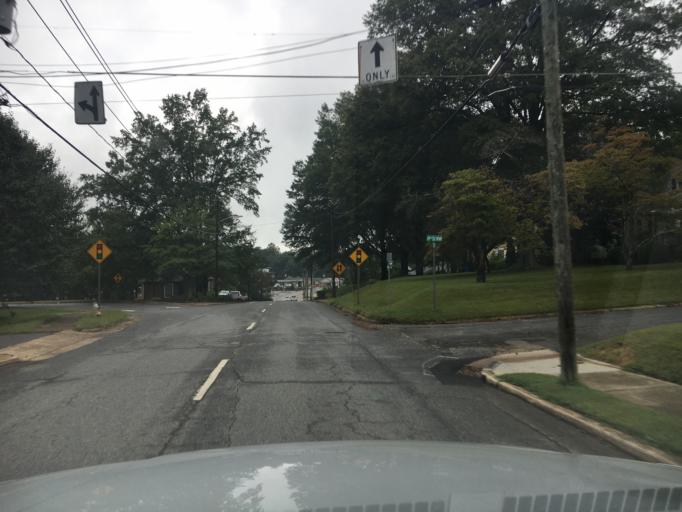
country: US
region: North Carolina
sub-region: Catawba County
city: Hickory
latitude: 35.7359
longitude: -81.3500
